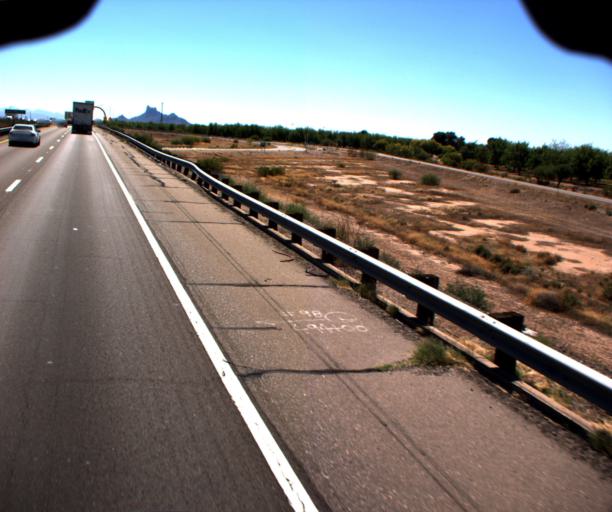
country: US
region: Arizona
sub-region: Pinal County
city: Eloy
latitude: 32.7240
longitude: -111.5173
